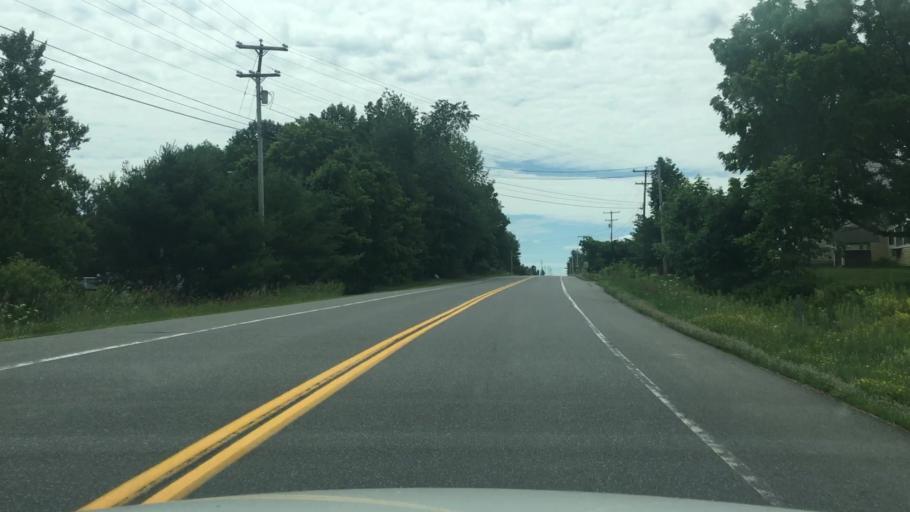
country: US
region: Maine
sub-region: Waldo County
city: Troy
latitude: 44.5610
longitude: -69.2716
